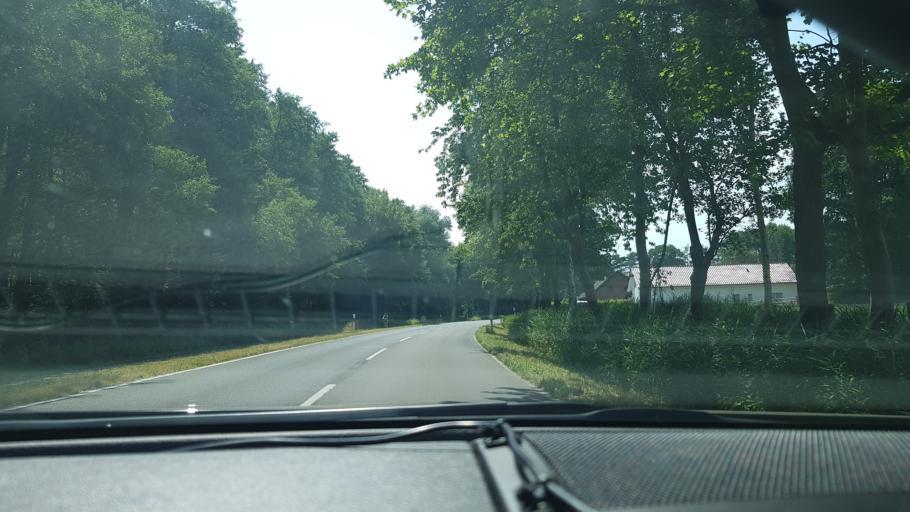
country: DE
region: North Rhine-Westphalia
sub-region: Regierungsbezirk Dusseldorf
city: Bruggen
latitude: 51.2251
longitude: 6.1881
